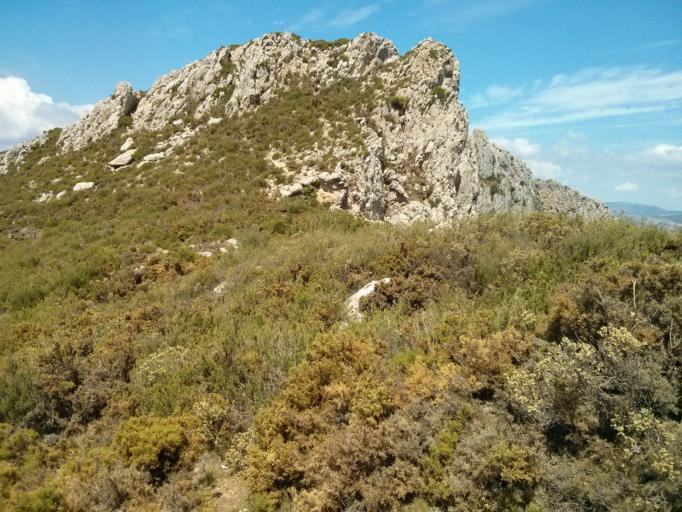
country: ES
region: Valencia
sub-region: Provincia de Alicante
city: Bolulla
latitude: 38.6621
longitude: -0.0637
